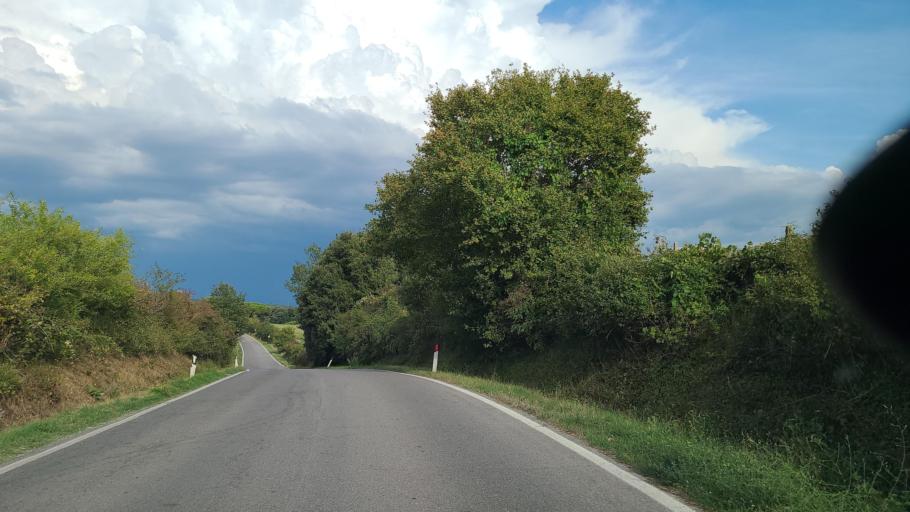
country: IT
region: Tuscany
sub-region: Province of Florence
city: Gambassi Terme
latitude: 43.4806
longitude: 10.9560
